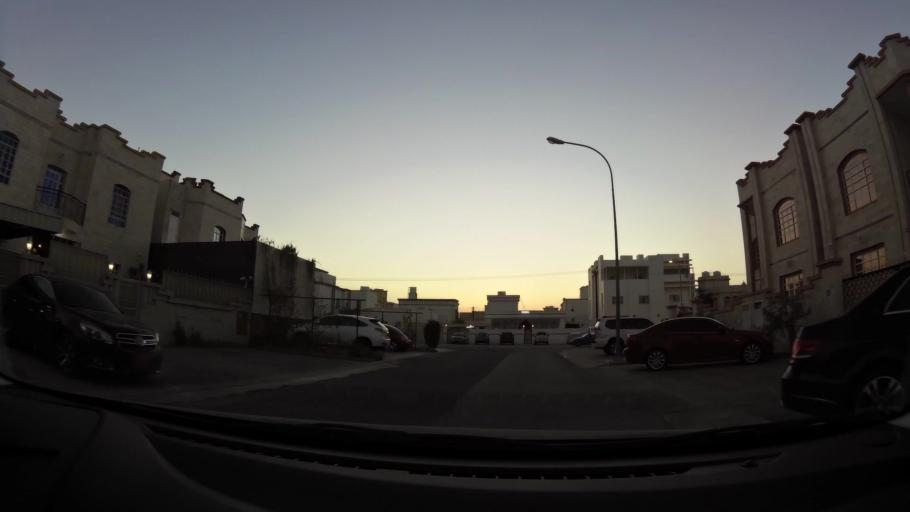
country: OM
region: Muhafazat Masqat
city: As Sib al Jadidah
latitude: 23.6008
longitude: 58.2349
